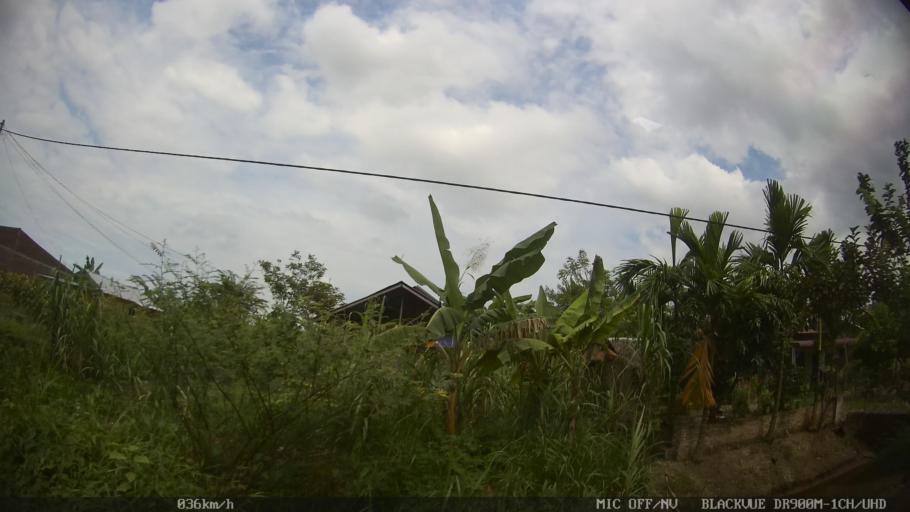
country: ID
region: North Sumatra
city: Sunggal
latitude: 3.6332
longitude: 98.6062
